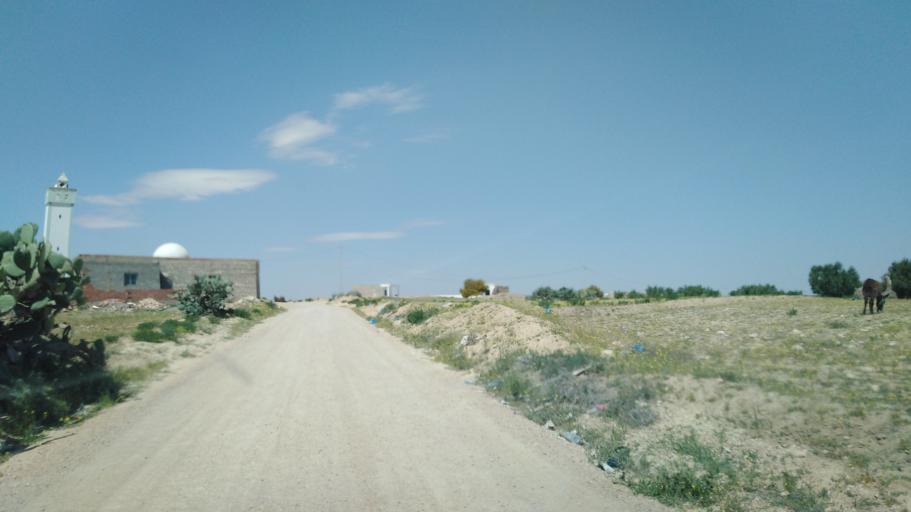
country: TN
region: Safaqis
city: Sfax
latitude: 34.7594
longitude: 10.5269
